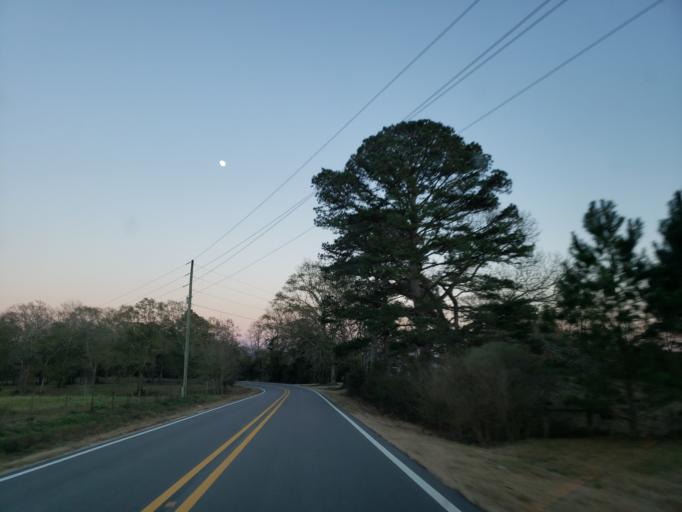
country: US
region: Mississippi
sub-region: Jones County
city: Ellisville
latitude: 31.5756
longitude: -89.2873
